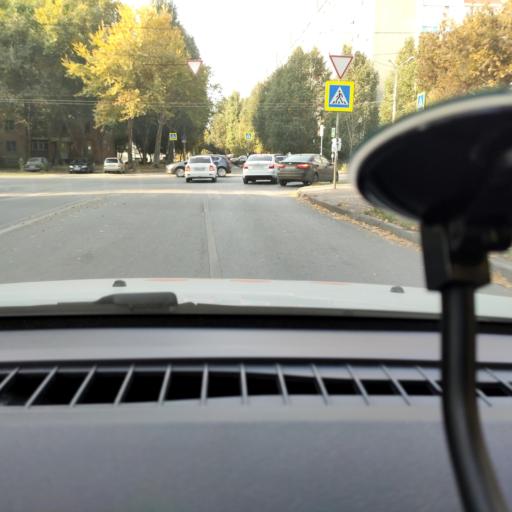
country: RU
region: Samara
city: Samara
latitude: 53.2306
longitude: 50.2521
